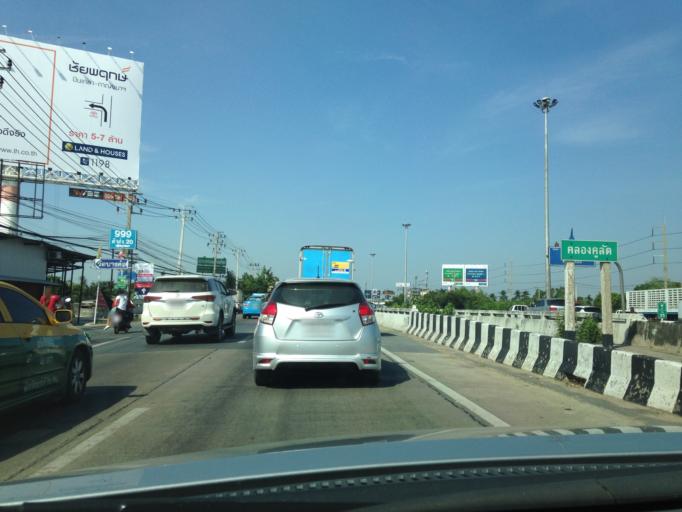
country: TH
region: Nonthaburi
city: Bang Yai
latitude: 13.8265
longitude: 100.4126
